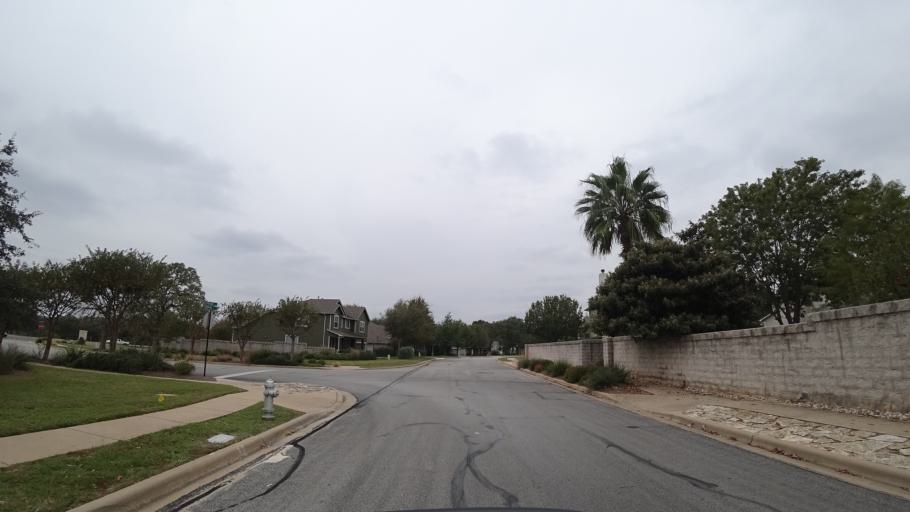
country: US
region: Texas
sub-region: Travis County
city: Shady Hollow
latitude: 30.2040
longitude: -97.8840
